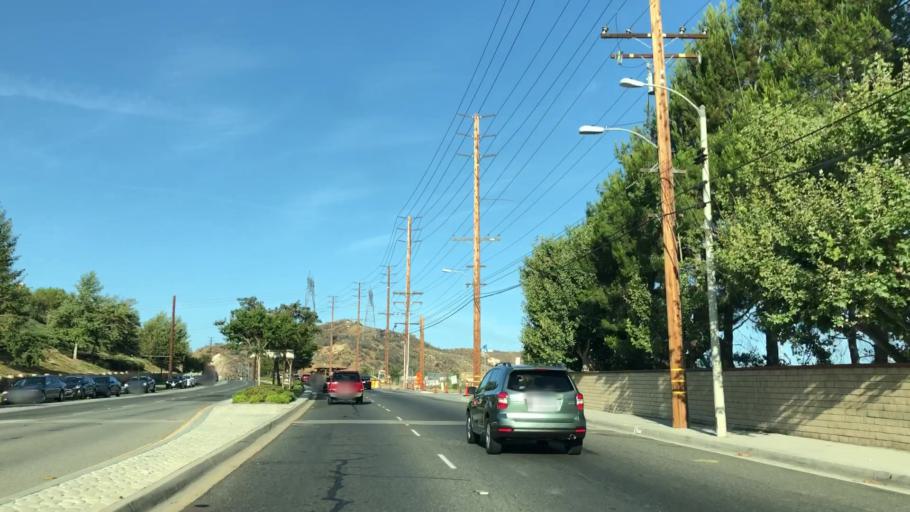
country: US
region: California
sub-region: Los Angeles County
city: Santa Clarita
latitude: 34.3975
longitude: -118.4815
